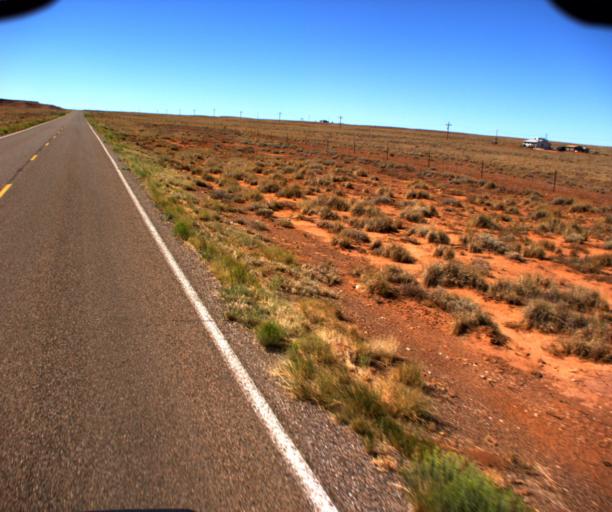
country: US
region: Arizona
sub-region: Coconino County
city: LeChee
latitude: 35.2116
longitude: -110.9502
